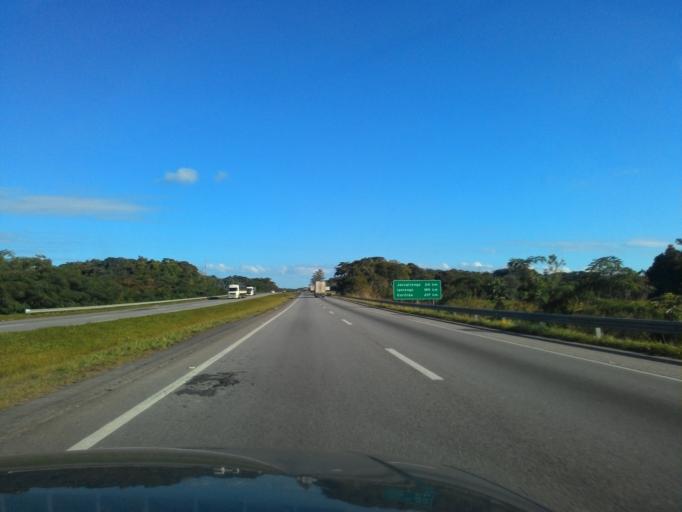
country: BR
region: Sao Paulo
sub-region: Registro
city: Registro
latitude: -24.5474
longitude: -47.8627
